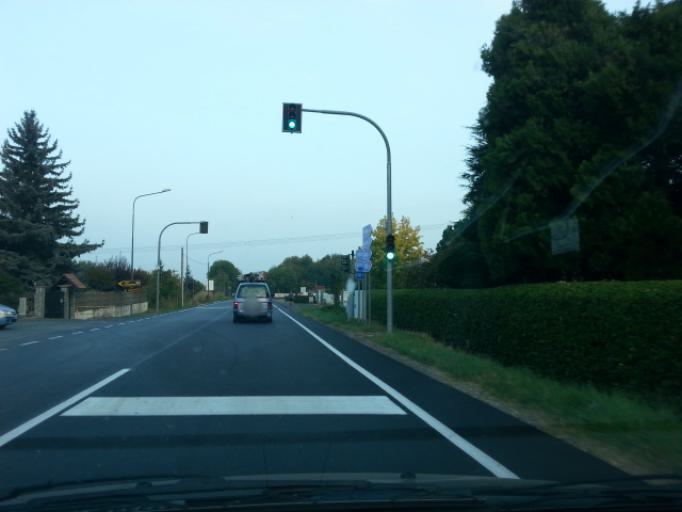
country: IT
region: Piedmont
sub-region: Provincia di Torino
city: Sangano
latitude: 45.0326
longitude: 7.4362
